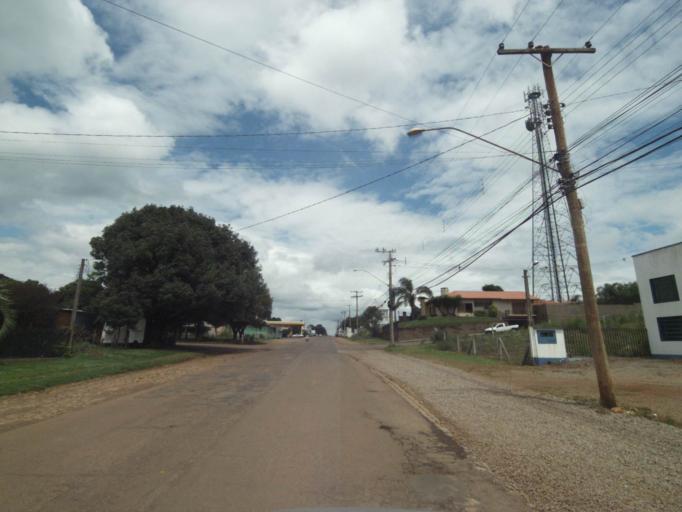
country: BR
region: Rio Grande do Sul
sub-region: Lagoa Vermelha
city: Lagoa Vermelha
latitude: -28.2185
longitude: -51.5162
